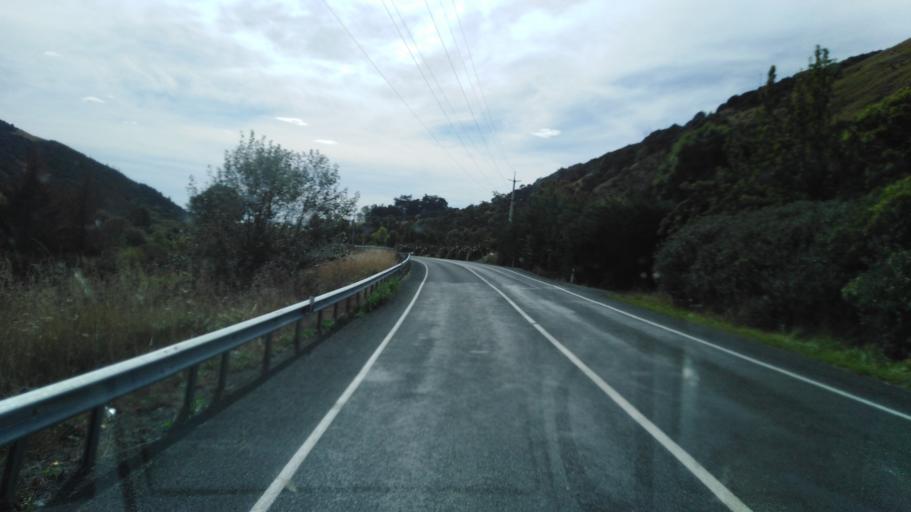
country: NZ
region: Canterbury
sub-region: Kaikoura District
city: Kaikoura
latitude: -42.5208
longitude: 173.4903
